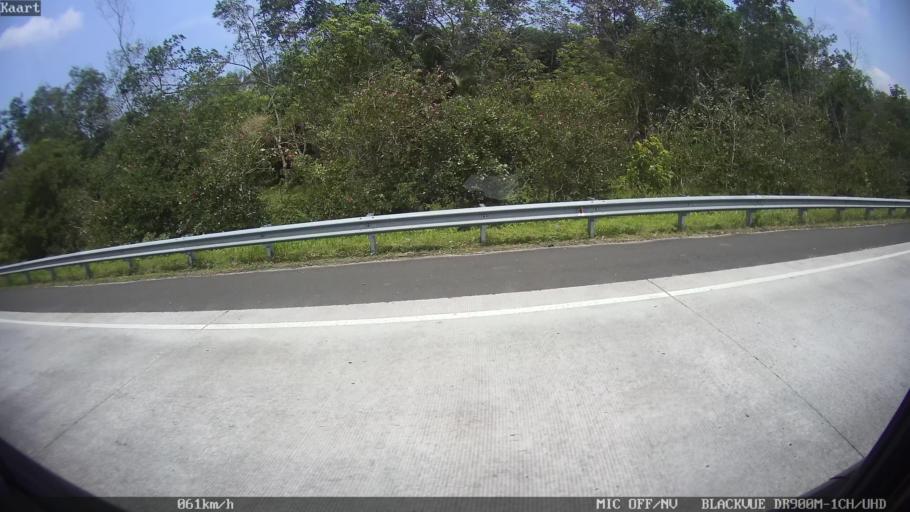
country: ID
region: Lampung
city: Kedaton
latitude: -5.3583
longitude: 105.3244
